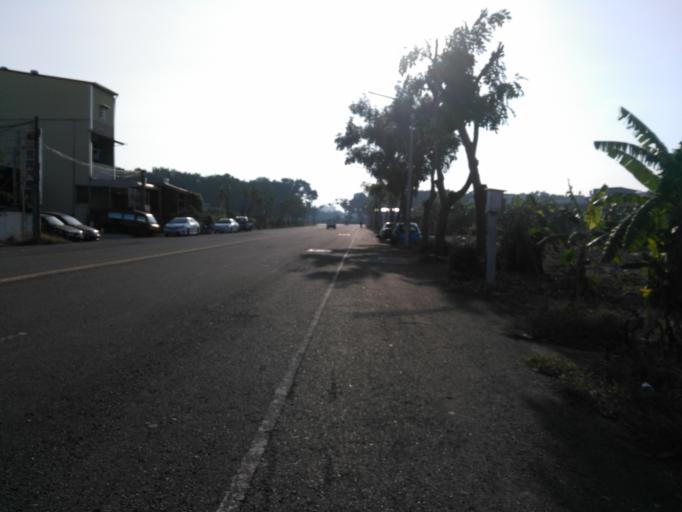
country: TW
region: Taiwan
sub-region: Chiayi
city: Jiayi Shi
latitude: 23.4720
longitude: 120.4195
